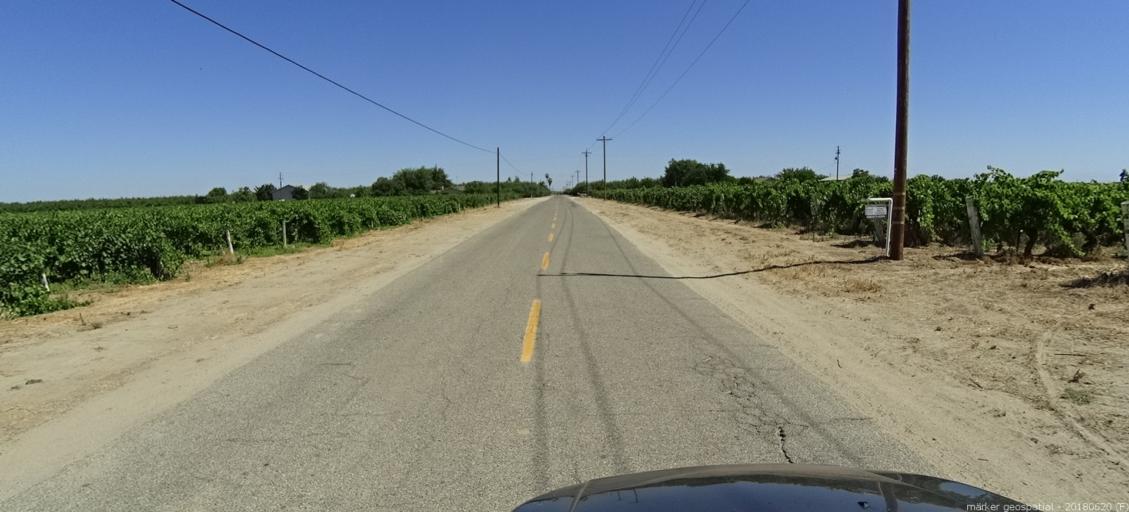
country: US
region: California
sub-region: Madera County
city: Parkwood
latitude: 36.9037
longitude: -120.0104
